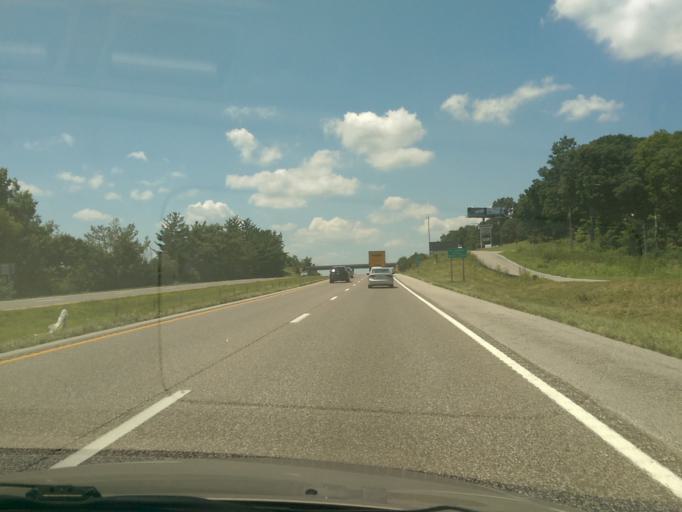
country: US
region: Missouri
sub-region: Boone County
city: Columbia
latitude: 38.9708
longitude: -92.3981
